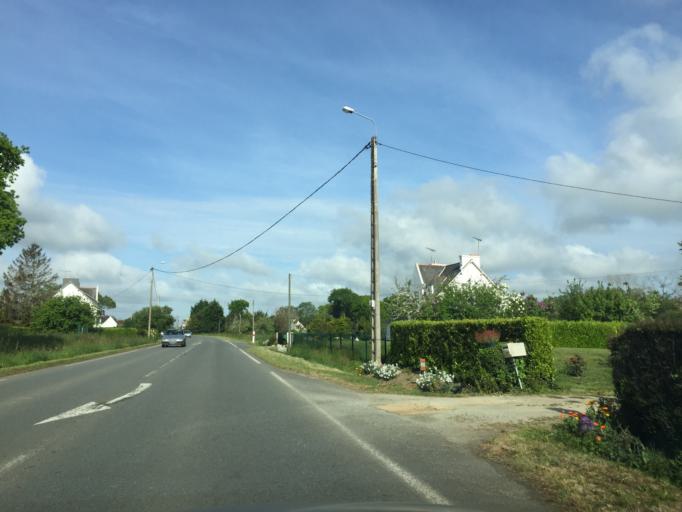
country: FR
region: Brittany
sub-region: Departement des Cotes-d'Armor
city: Saint-Cast-le-Guildo
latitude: 48.5937
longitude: -2.2524
